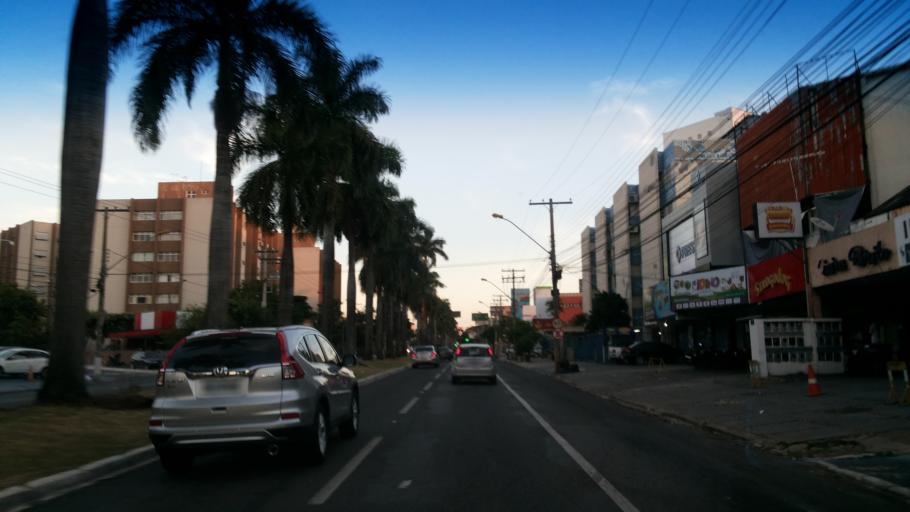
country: BR
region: Goias
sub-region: Goiania
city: Goiania
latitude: -16.6991
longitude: -49.2644
